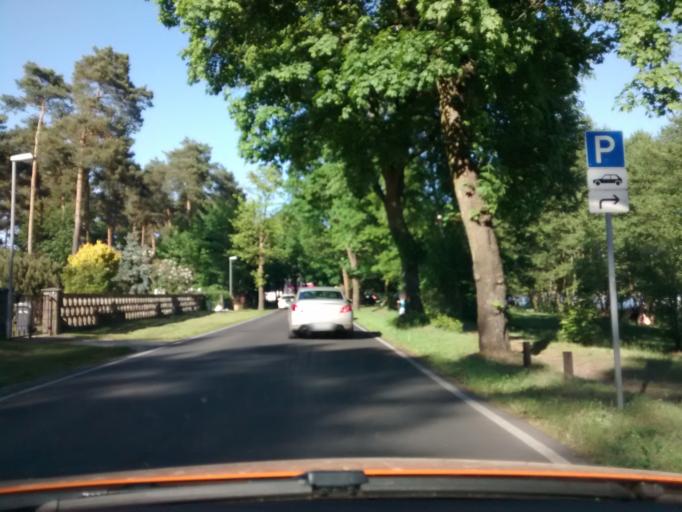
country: DE
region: Brandenburg
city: Bad Saarow
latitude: 52.3153
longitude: 14.0699
